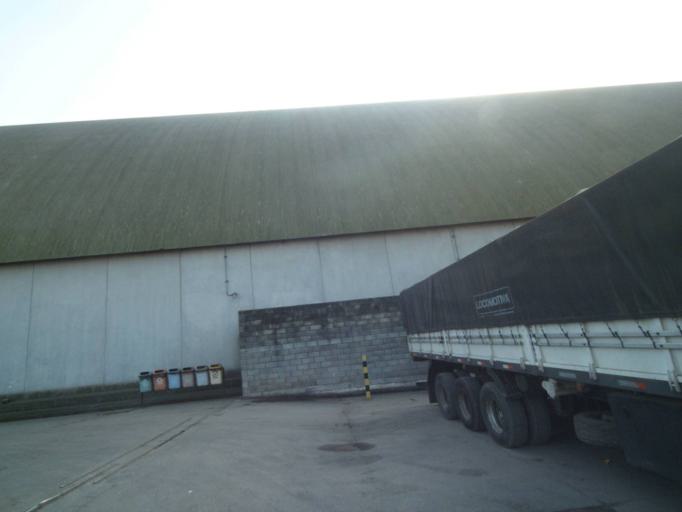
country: BR
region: Parana
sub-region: Paranagua
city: Paranagua
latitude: -25.5096
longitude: -48.5079
